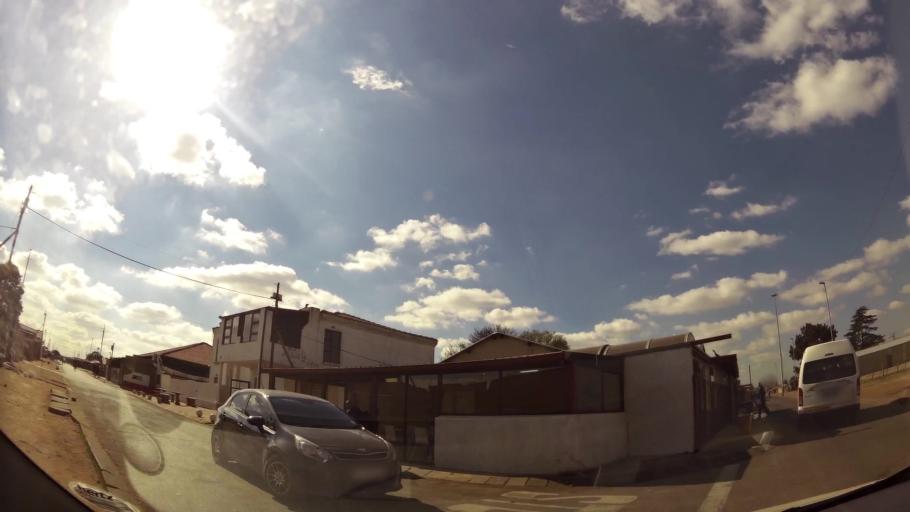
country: ZA
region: Gauteng
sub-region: West Rand District Municipality
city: Krugersdorp
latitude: -26.1427
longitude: 27.7958
